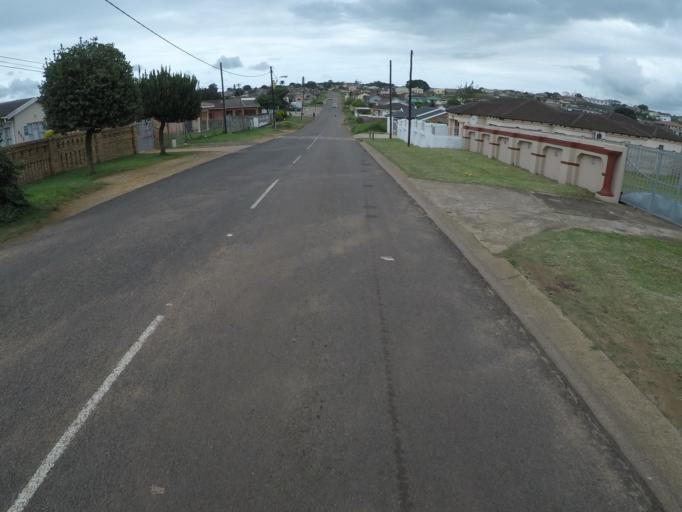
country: ZA
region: KwaZulu-Natal
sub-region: uThungulu District Municipality
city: Empangeni
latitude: -28.7810
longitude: 31.8500
